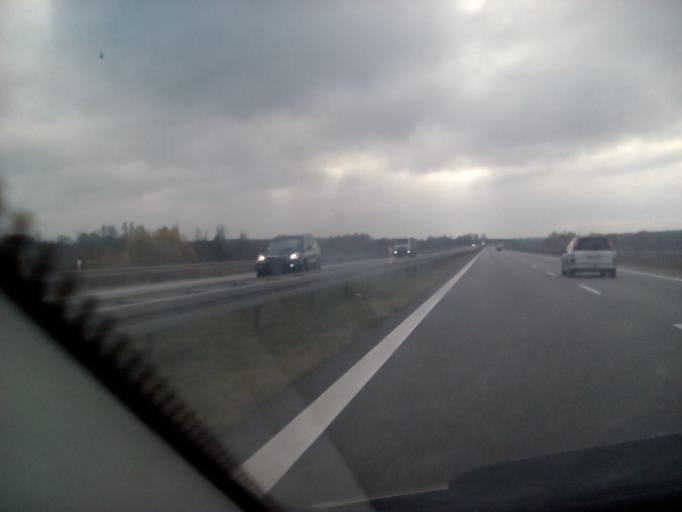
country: PL
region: Masovian Voivodeship
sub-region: Powiat bialobrzeski
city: Bialobrzegi
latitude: 51.6620
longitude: 20.9597
